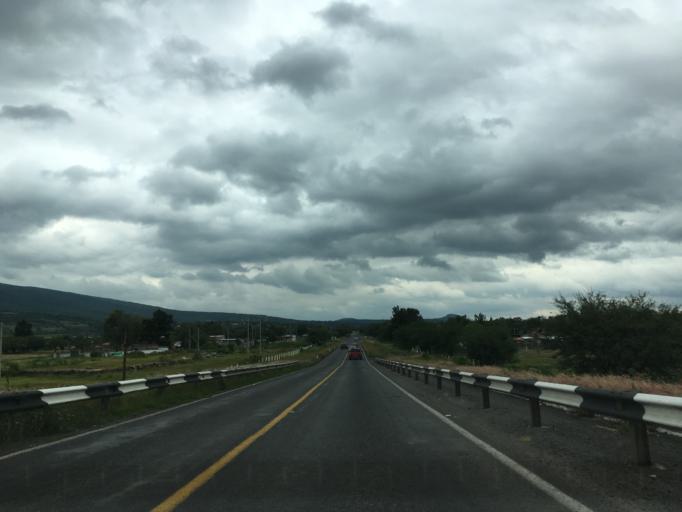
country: MX
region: Michoacan
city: Cuitzeo del Porvenir
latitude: 19.9882
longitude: -101.1493
